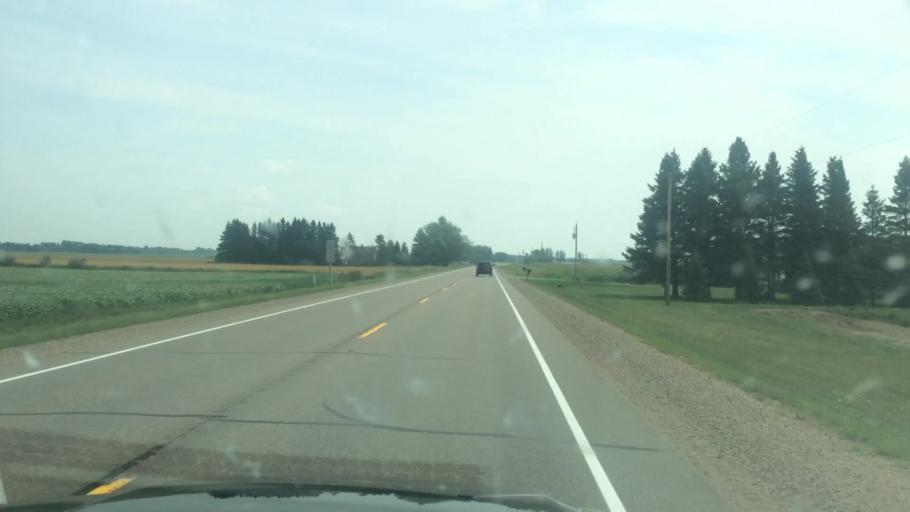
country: US
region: Wisconsin
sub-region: Langlade County
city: Antigo
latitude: 45.1400
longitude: -89.2057
